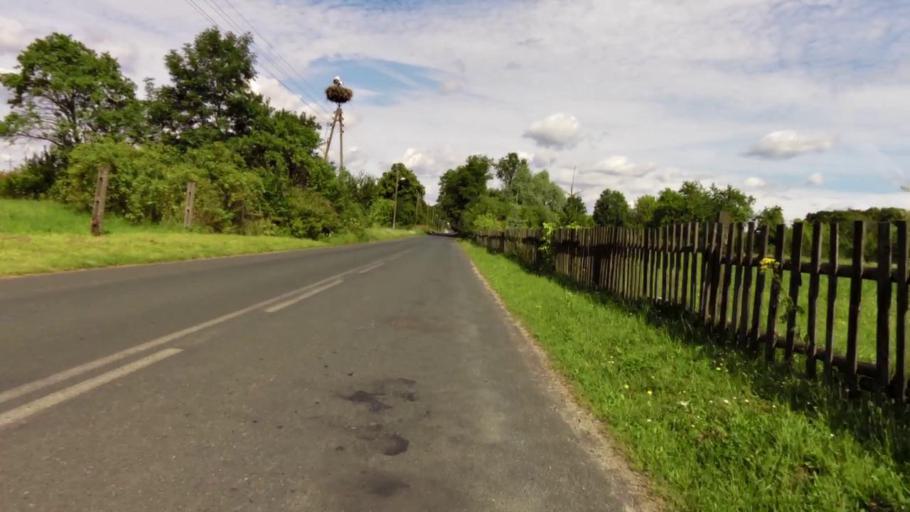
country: PL
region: West Pomeranian Voivodeship
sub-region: Powiat stargardzki
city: Dobrzany
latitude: 53.4060
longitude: 15.4311
